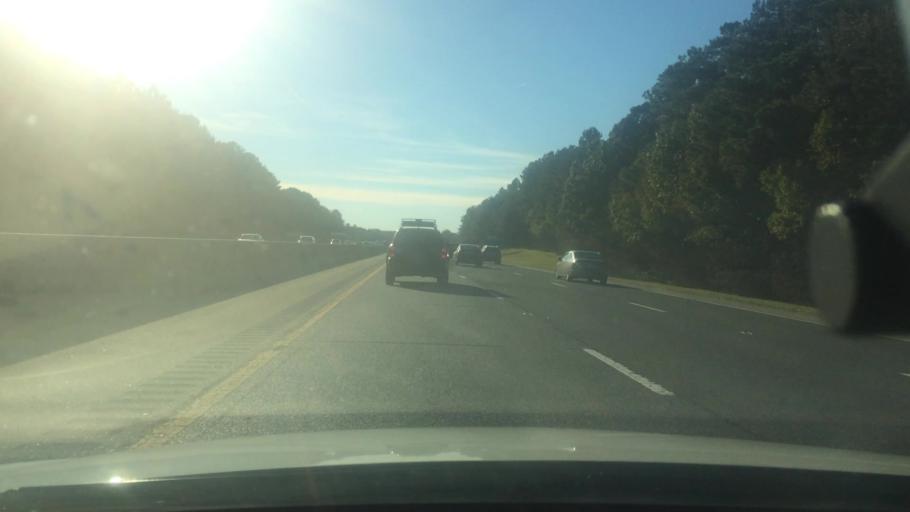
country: US
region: North Carolina
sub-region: Durham County
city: Durham
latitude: 35.9059
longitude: -78.9509
